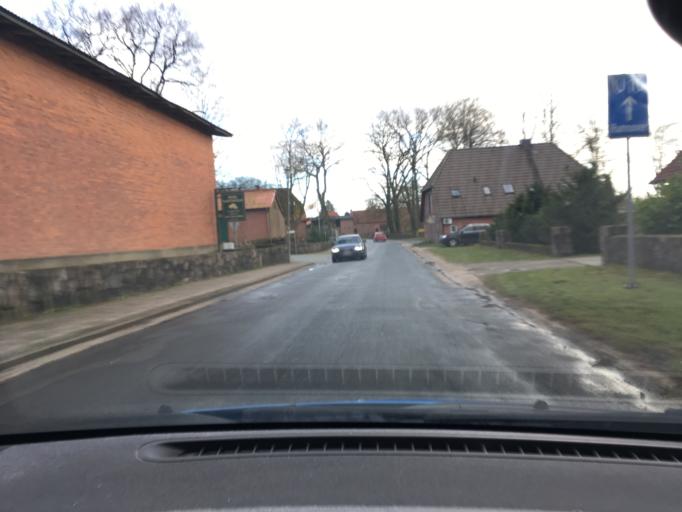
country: DE
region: Lower Saxony
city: Egestorf
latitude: 53.2121
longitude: 10.0303
